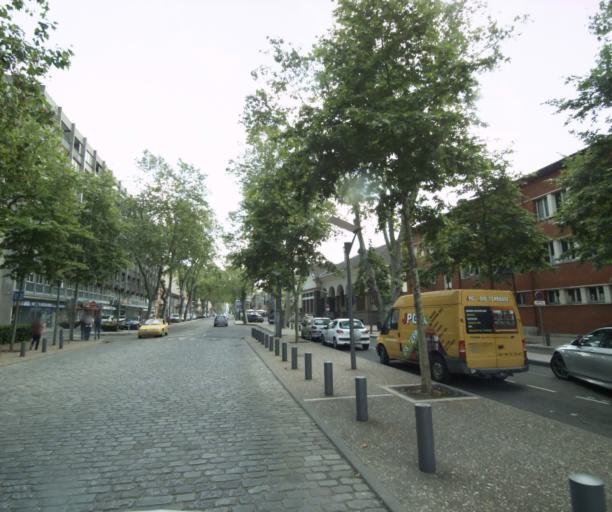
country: FR
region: Midi-Pyrenees
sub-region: Departement du Tarn-et-Garonne
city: Montauban
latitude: 44.0174
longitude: 1.3591
